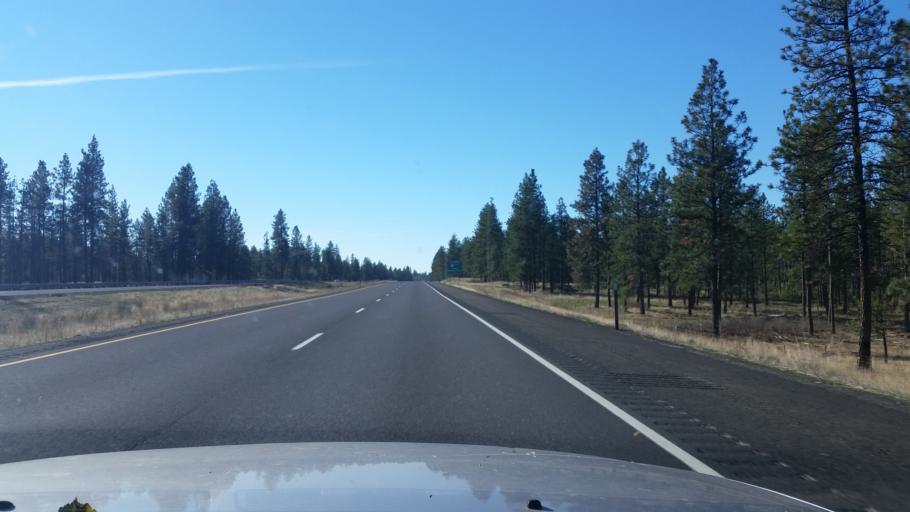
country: US
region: Washington
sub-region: Spokane County
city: Medical Lake
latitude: 47.5192
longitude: -117.6703
